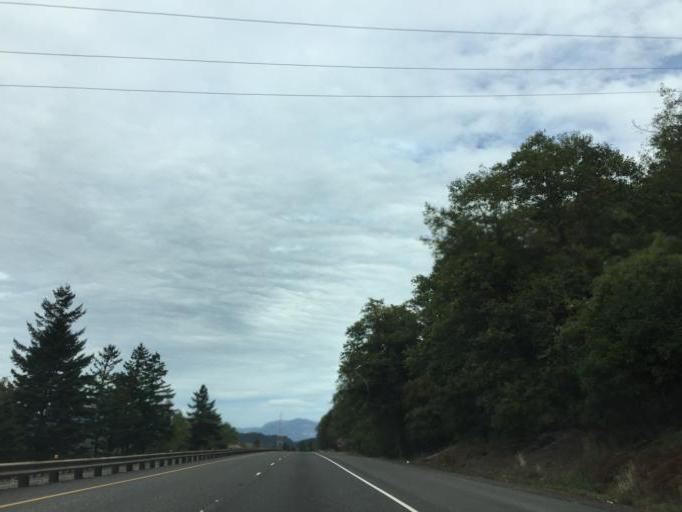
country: US
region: Oregon
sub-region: Hood River County
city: Cascade Locks
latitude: 45.6281
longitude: -121.9671
